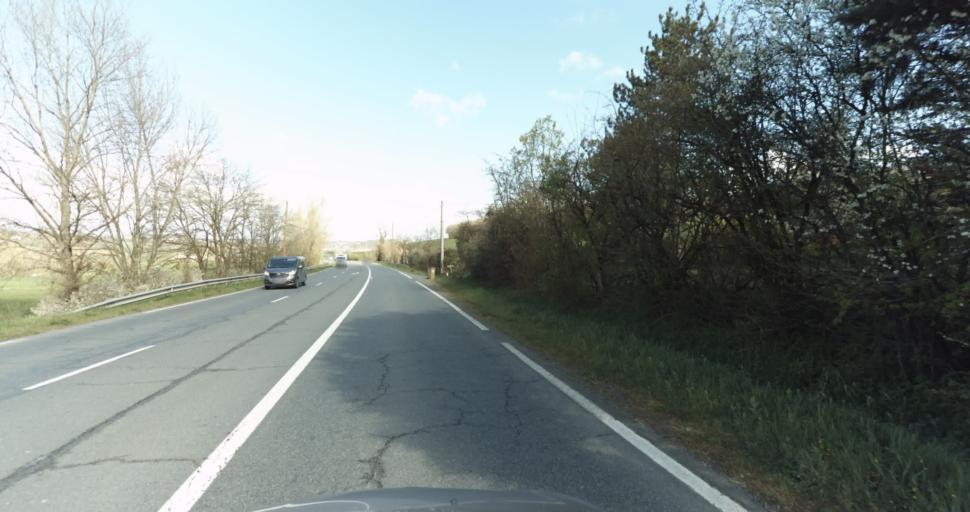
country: FR
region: Midi-Pyrenees
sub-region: Departement du Tarn
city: Puygouzon
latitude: 43.8674
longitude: 2.1859
